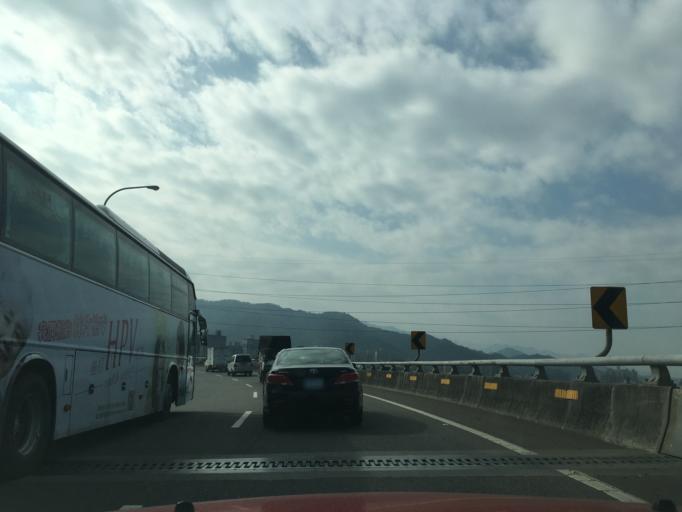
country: TW
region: Taipei
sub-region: Taipei
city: Banqiao
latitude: 24.9733
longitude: 121.4324
